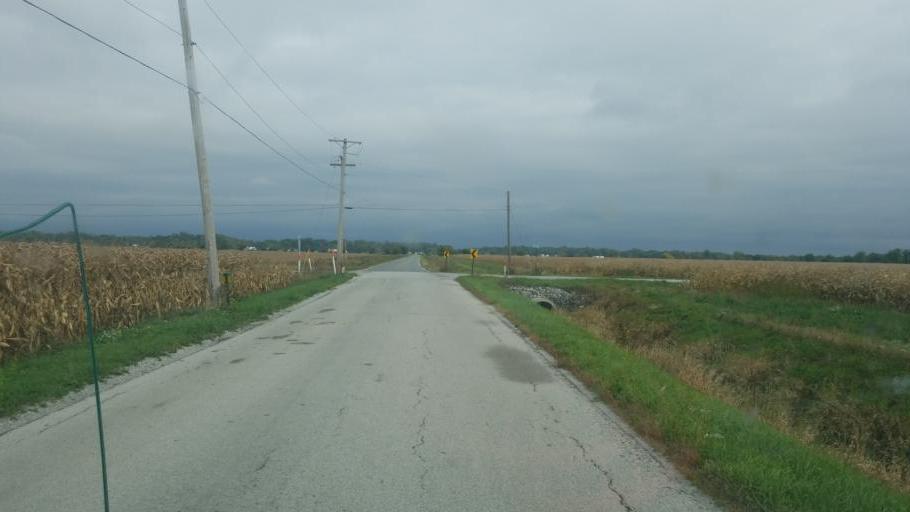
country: US
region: Ohio
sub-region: Wood County
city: Bowling Green
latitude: 41.3420
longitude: -83.6697
